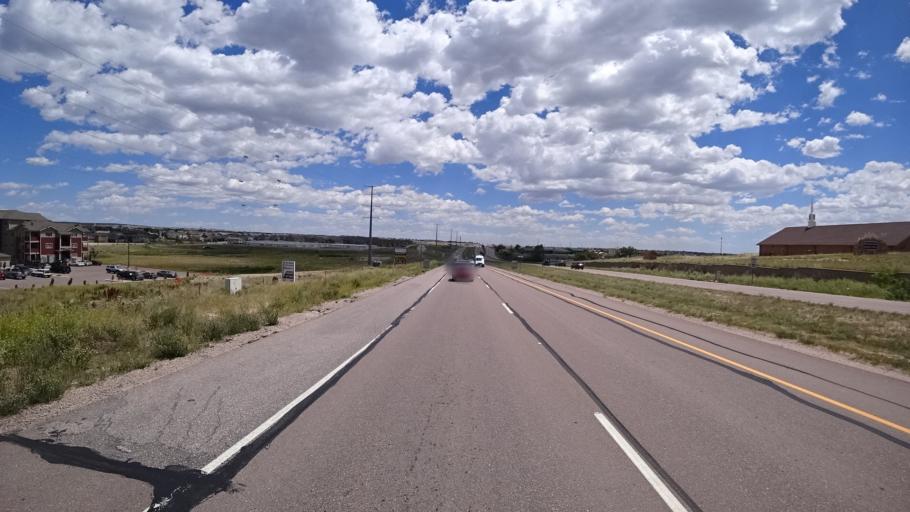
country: US
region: Colorado
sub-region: El Paso County
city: Black Forest
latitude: 38.9411
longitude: -104.6989
